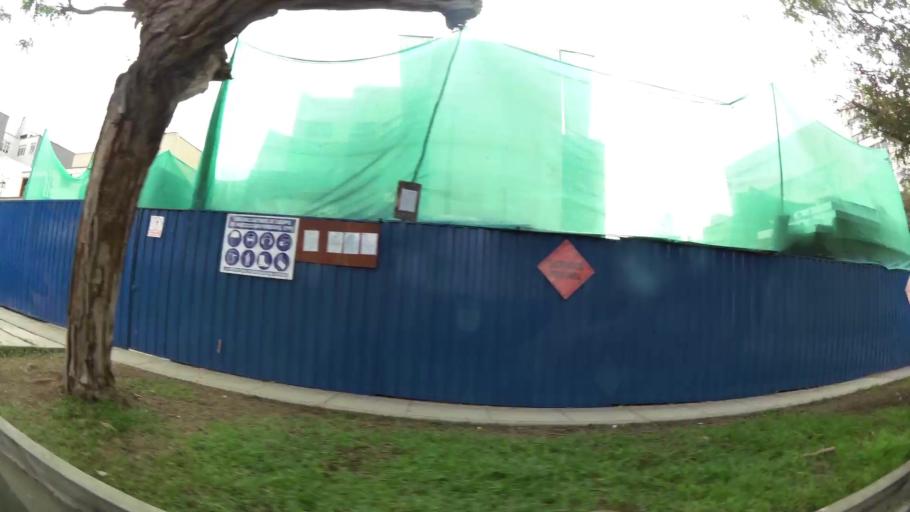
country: PE
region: Lima
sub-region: Lima
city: San Isidro
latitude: -12.1043
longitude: -77.0491
